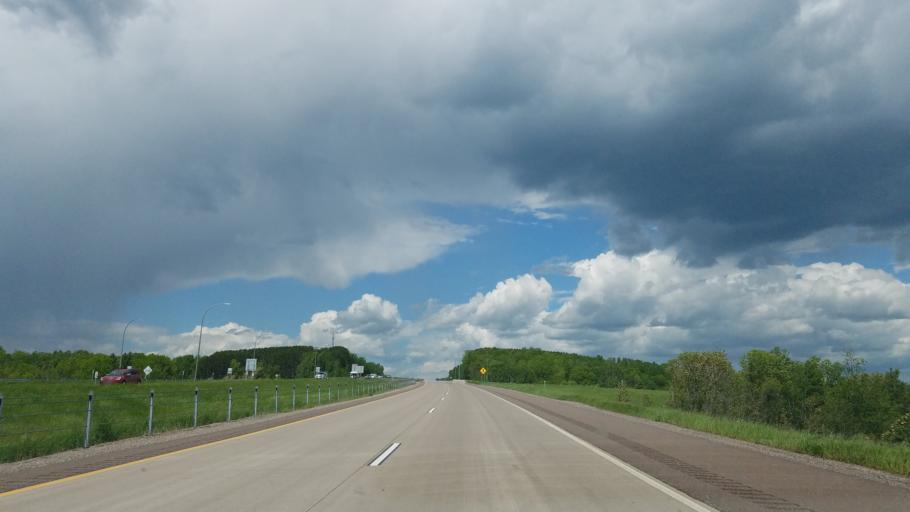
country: US
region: Minnesota
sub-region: Carlton County
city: Moose Lake
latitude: 46.4505
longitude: -92.7315
